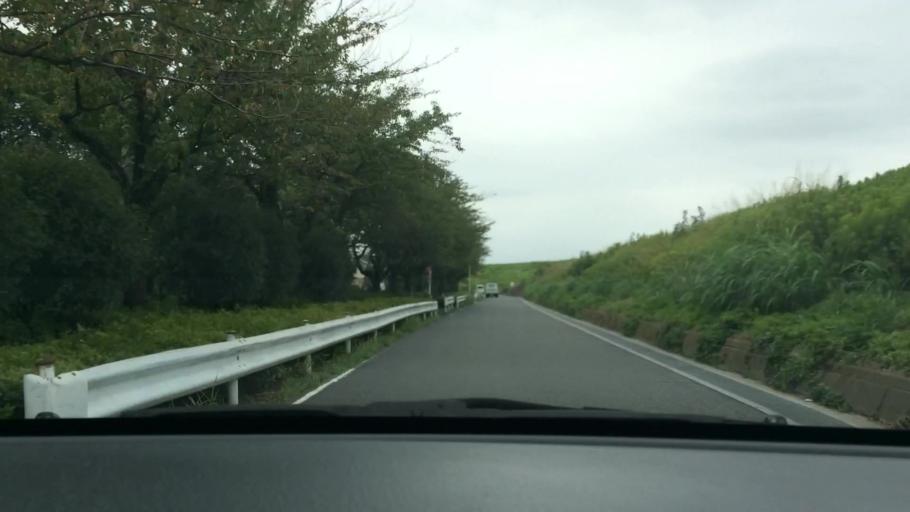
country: JP
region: Chiba
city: Matsudo
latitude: 35.8116
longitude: 139.8863
